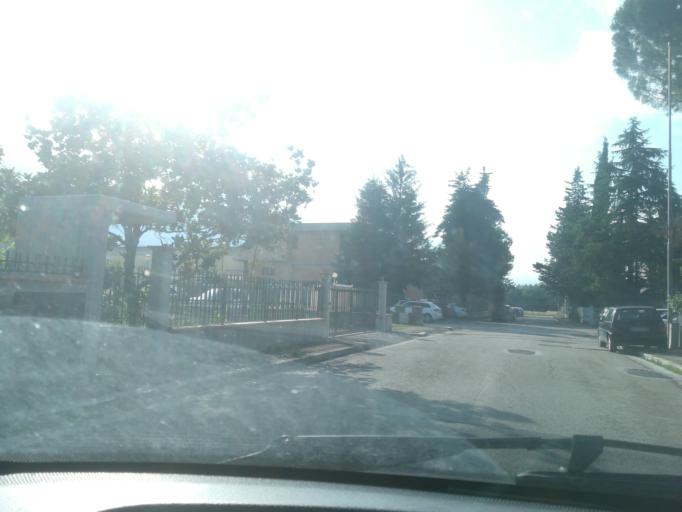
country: IT
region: The Marches
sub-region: Provincia di Macerata
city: Villa Potenza
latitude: 43.3168
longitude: 13.4208
